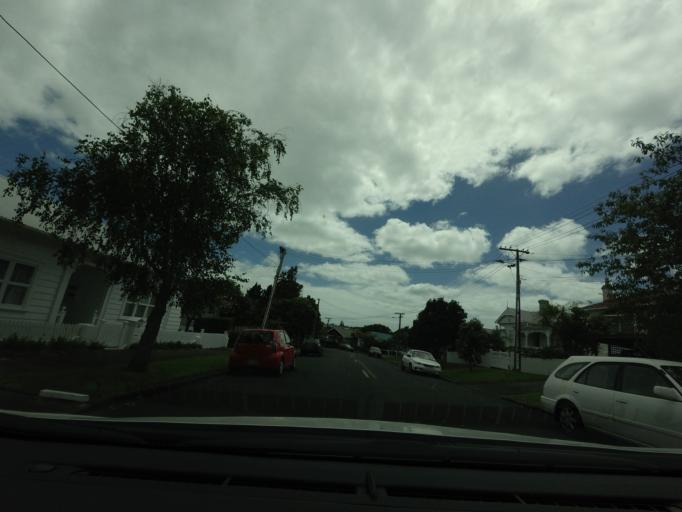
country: NZ
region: Auckland
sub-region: Auckland
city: Auckland
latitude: -36.8713
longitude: 174.7335
